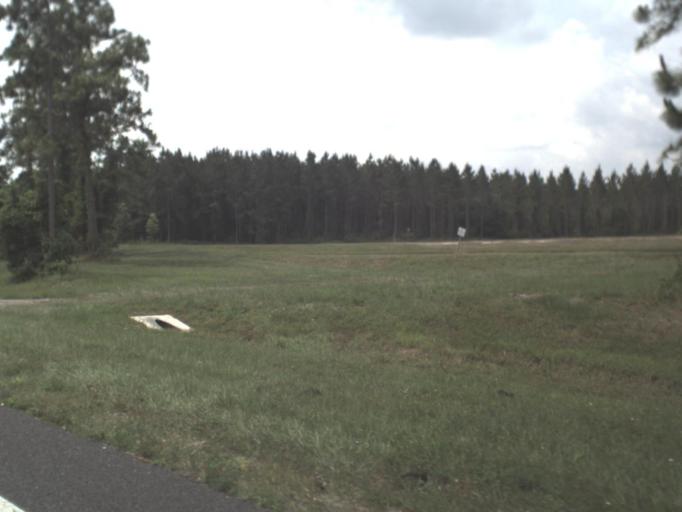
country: US
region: Florida
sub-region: Clay County
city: Green Cove Springs
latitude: 29.8957
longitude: -81.6715
